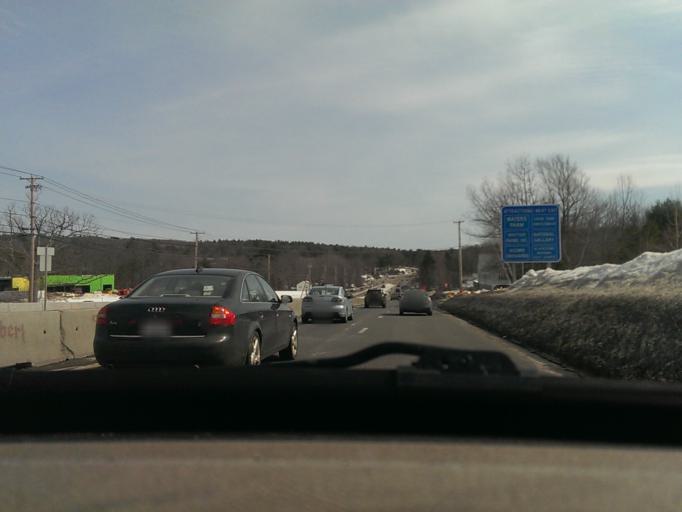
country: US
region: Massachusetts
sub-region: Worcester County
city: Sutton
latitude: 42.1604
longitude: -71.7370
